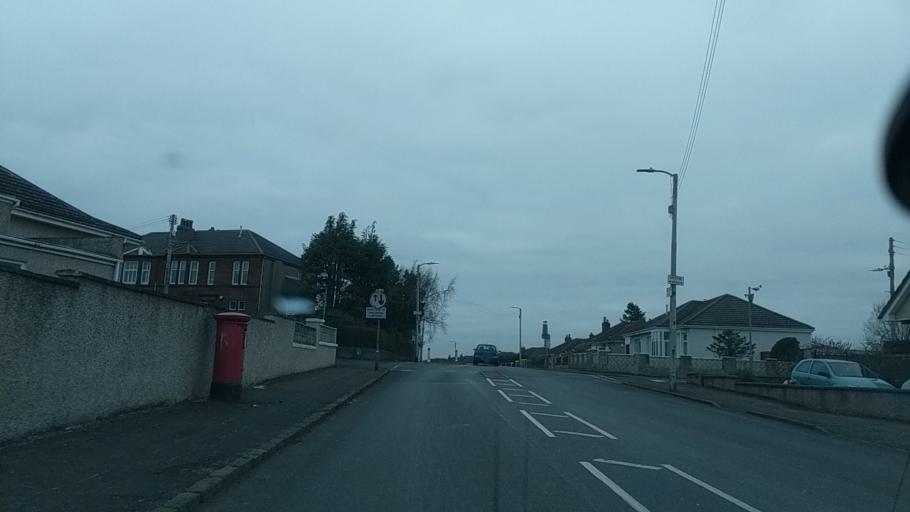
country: GB
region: Scotland
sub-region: South Lanarkshire
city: Rutherglen
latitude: 55.8199
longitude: -4.1937
